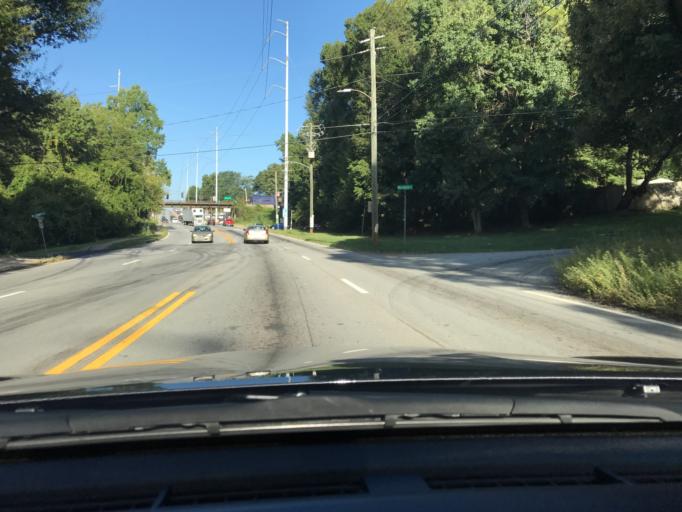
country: US
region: Georgia
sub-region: DeKalb County
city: Scottdale
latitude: 33.7934
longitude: -84.2617
